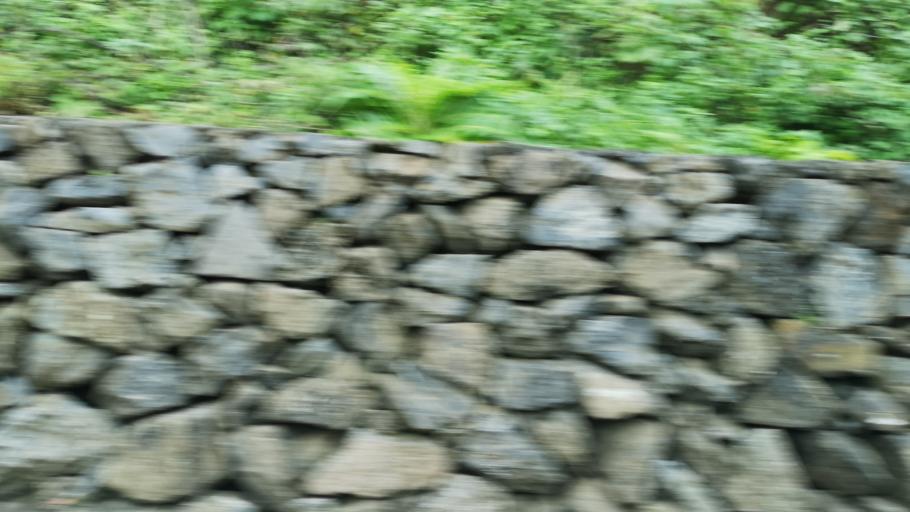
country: ES
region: Canary Islands
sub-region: Provincia de Santa Cruz de Tenerife
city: Hermigua
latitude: 28.1345
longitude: -17.1939
